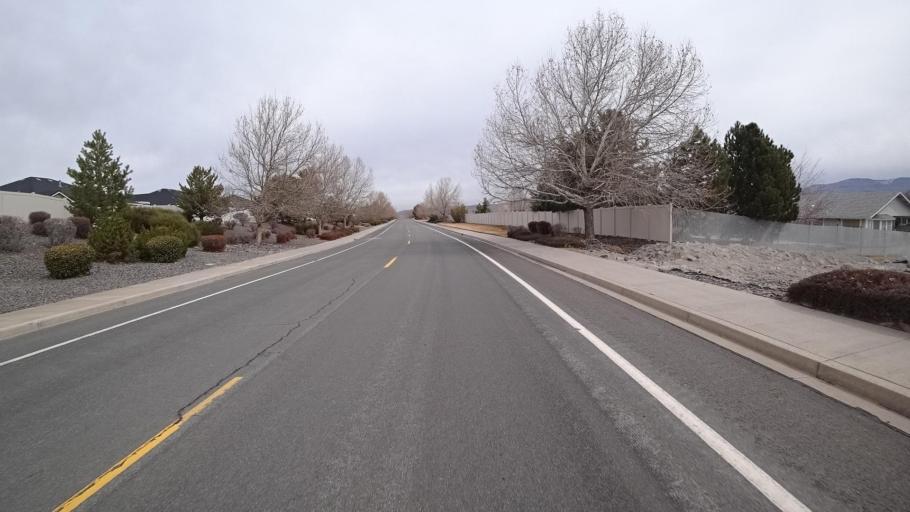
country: US
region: Nevada
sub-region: Washoe County
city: Spanish Springs
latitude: 39.6580
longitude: -119.7287
